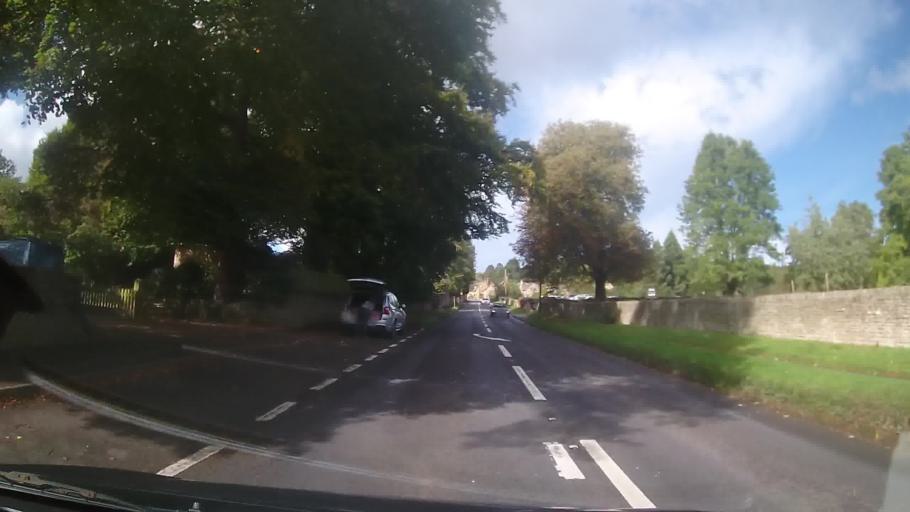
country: GB
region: England
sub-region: Gloucestershire
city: Moreton in Marsh
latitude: 51.9903
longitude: -1.7415
